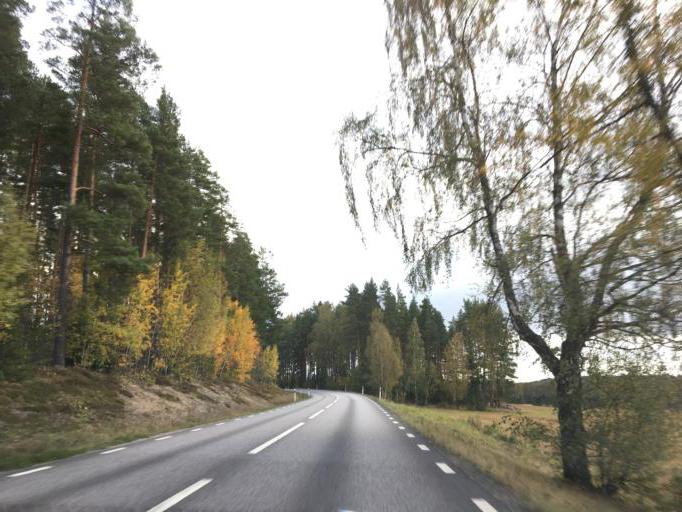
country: SE
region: Soedermanland
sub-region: Flens Kommun
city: Flen
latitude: 58.9159
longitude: 16.4302
